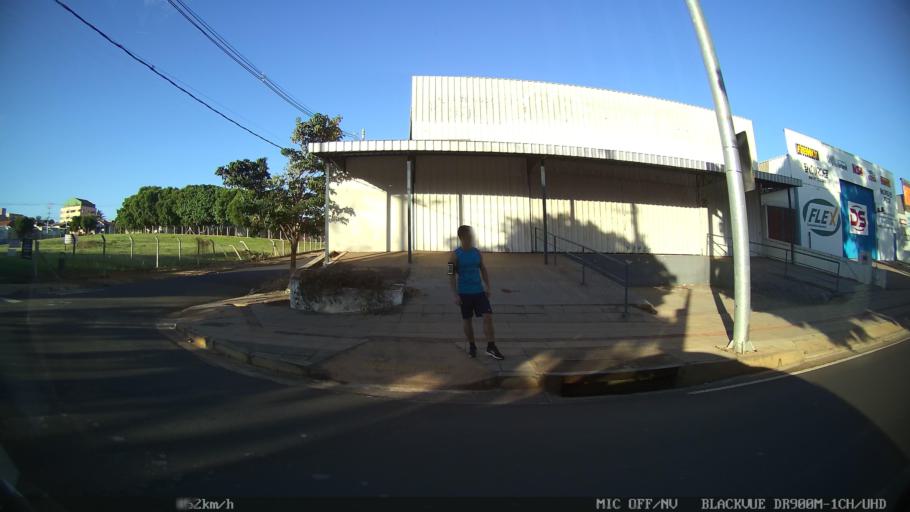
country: BR
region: Sao Paulo
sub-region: Sao Jose Do Rio Preto
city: Sao Jose do Rio Preto
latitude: -20.7928
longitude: -49.3758
